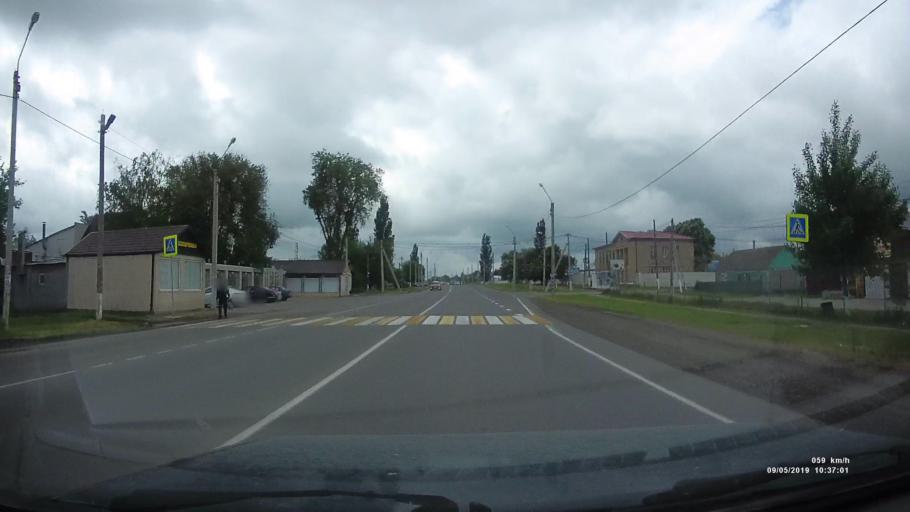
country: RU
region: Rostov
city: Peshkovo
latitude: 47.0237
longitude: 39.4048
